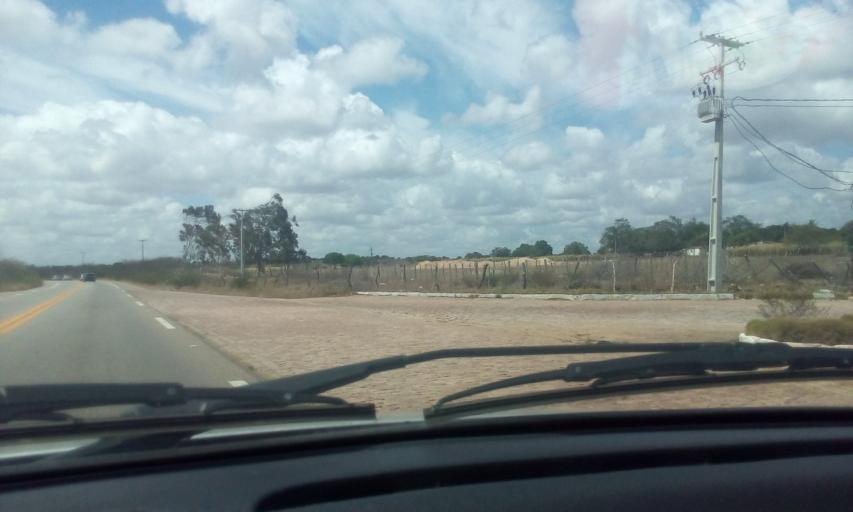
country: BR
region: Rio Grande do Norte
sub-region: Macaiba
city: Macaiba
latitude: -5.9365
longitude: -35.5488
